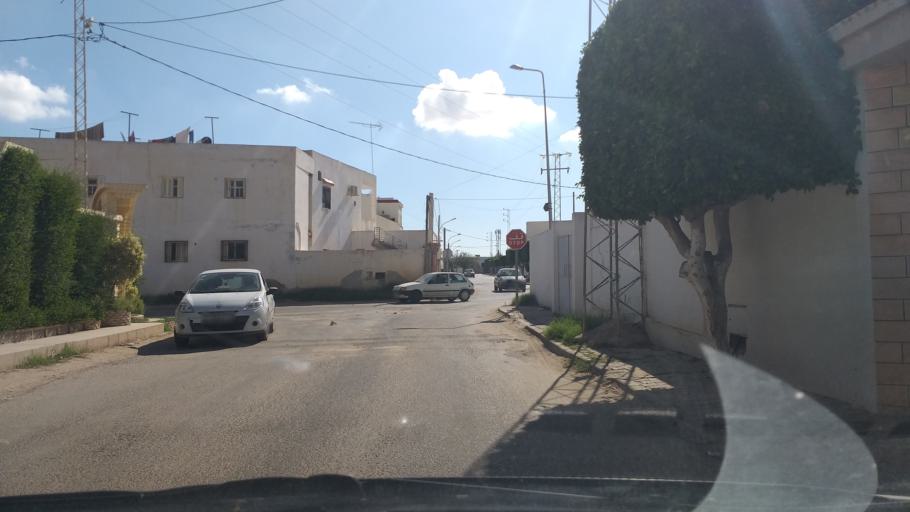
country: TN
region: Safaqis
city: Al Qarmadah
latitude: 34.8002
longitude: 10.7741
